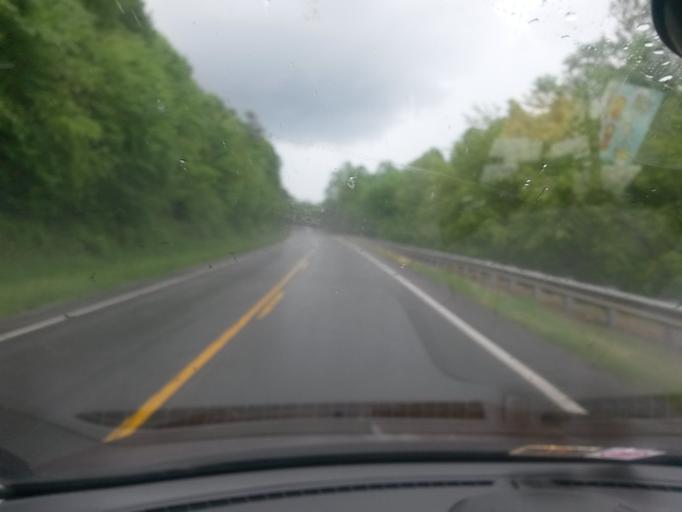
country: US
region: Virginia
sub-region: Floyd County
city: Floyd
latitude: 36.9671
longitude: -80.3778
